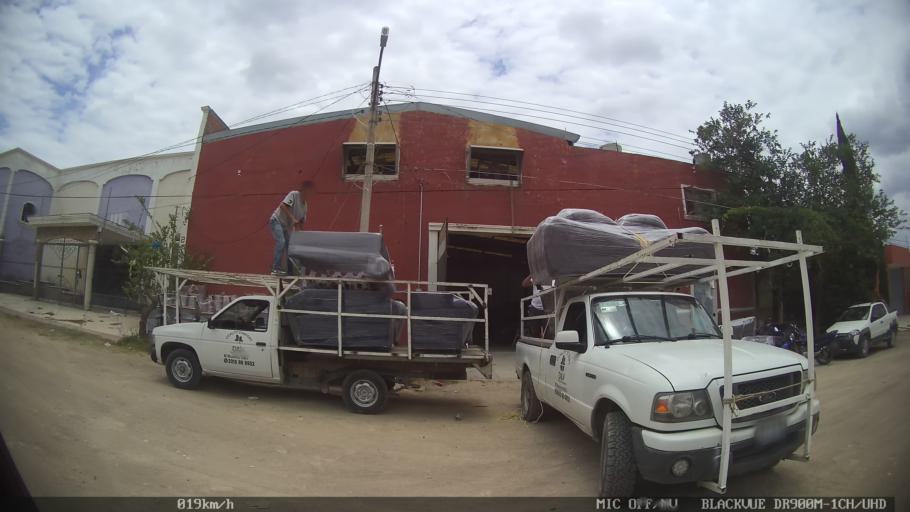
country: MX
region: Jalisco
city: Tlaquepaque
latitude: 20.6504
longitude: -103.2678
